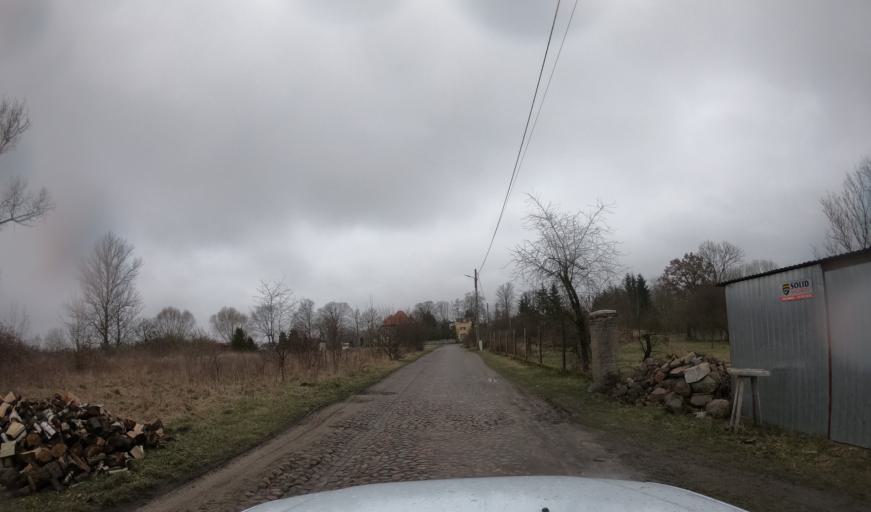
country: PL
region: West Pomeranian Voivodeship
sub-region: Powiat kamienski
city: Kamien Pomorski
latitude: 53.8923
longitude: 14.8271
